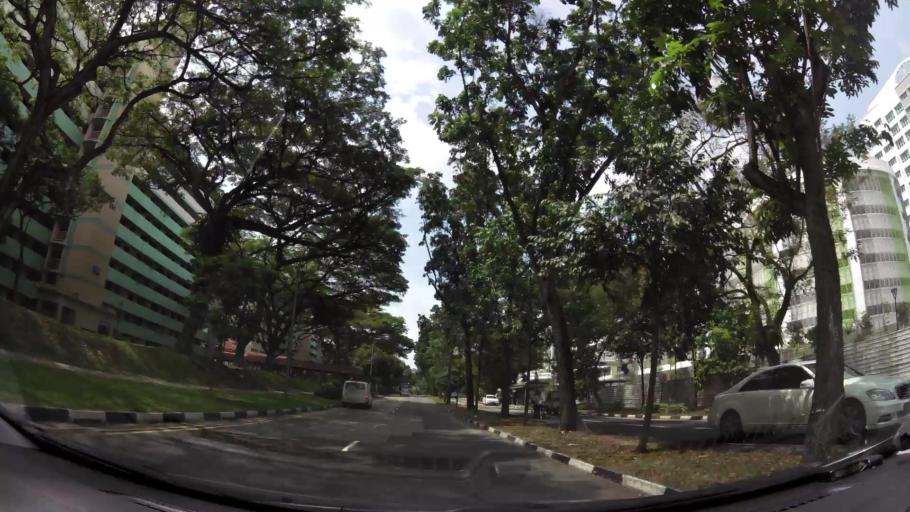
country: MY
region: Johor
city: Johor Bahru
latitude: 1.3500
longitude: 103.7129
